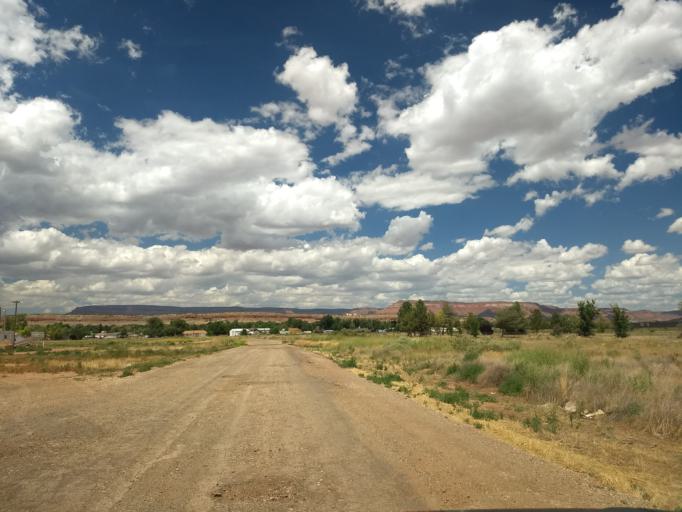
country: US
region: Arizona
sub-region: Coconino County
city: Fredonia
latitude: 36.9442
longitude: -112.5140
